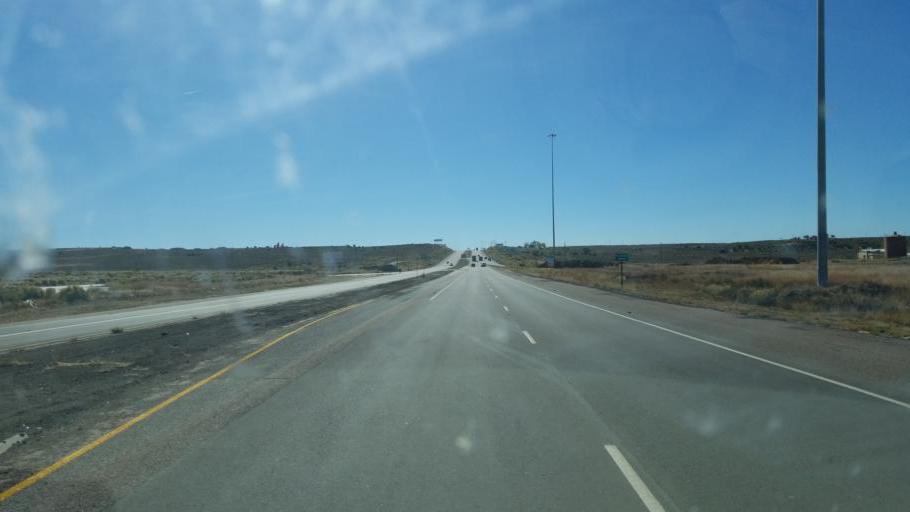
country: US
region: New Mexico
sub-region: McKinley County
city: Twin Lakes
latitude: 35.6265
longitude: -108.7813
